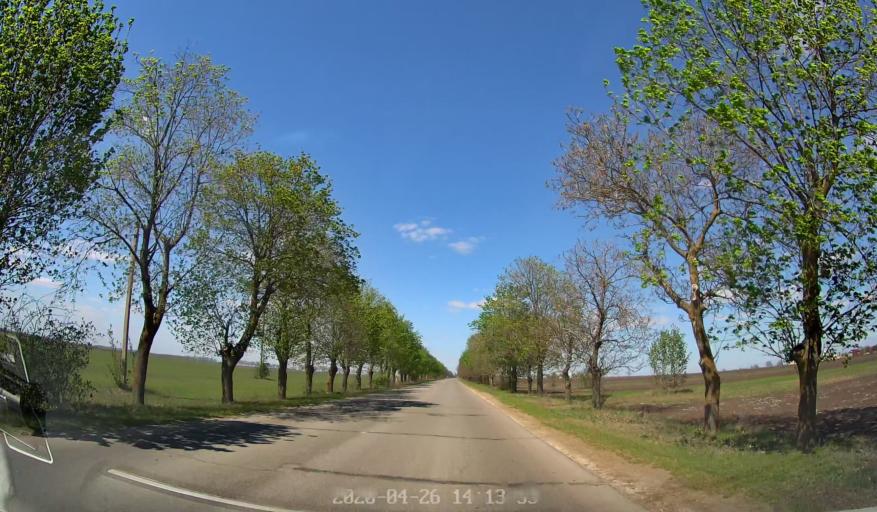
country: MD
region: Telenesti
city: Cocieri
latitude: 47.3148
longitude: 29.0563
